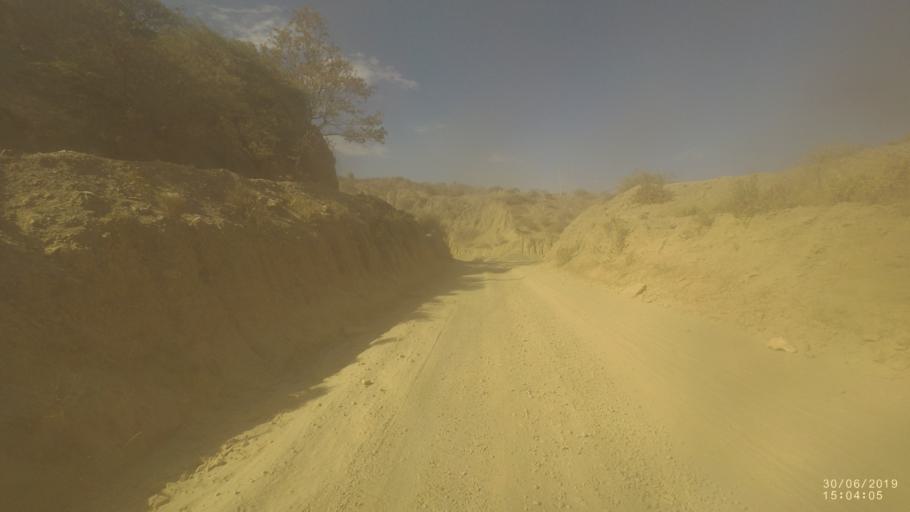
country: BO
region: Cochabamba
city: Irpa Irpa
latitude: -17.7316
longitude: -66.3227
